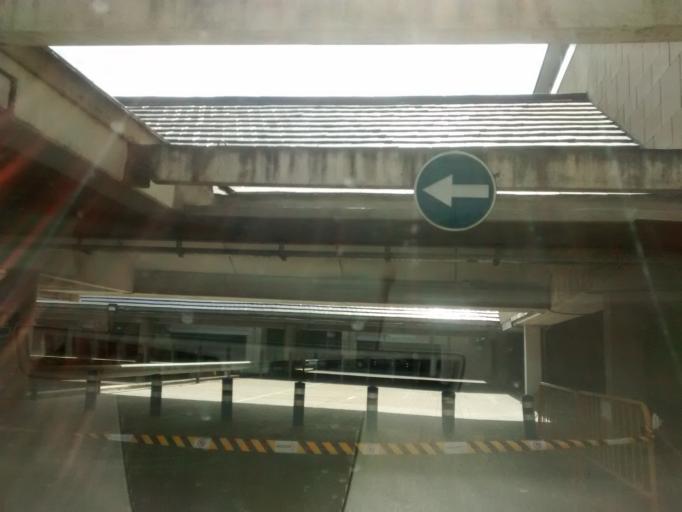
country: ES
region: Andalusia
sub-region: Provincia de Sevilla
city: Sevilla
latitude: 37.4234
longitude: -5.9013
